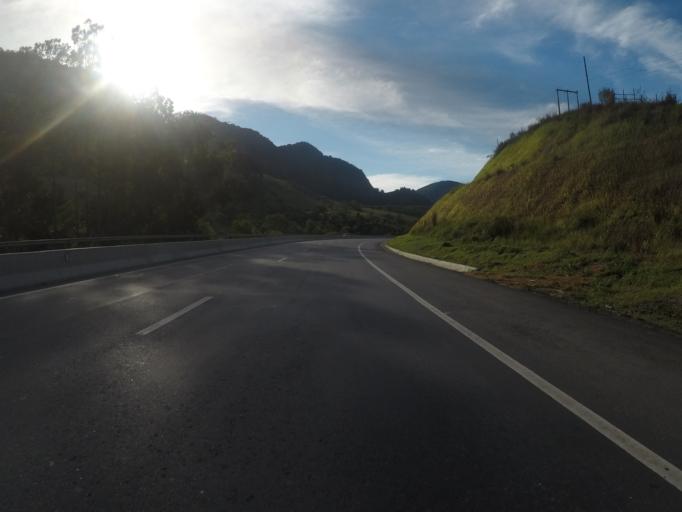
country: BR
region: Espirito Santo
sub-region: Ibiracu
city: Ibiracu
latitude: -19.8446
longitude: -40.3856
